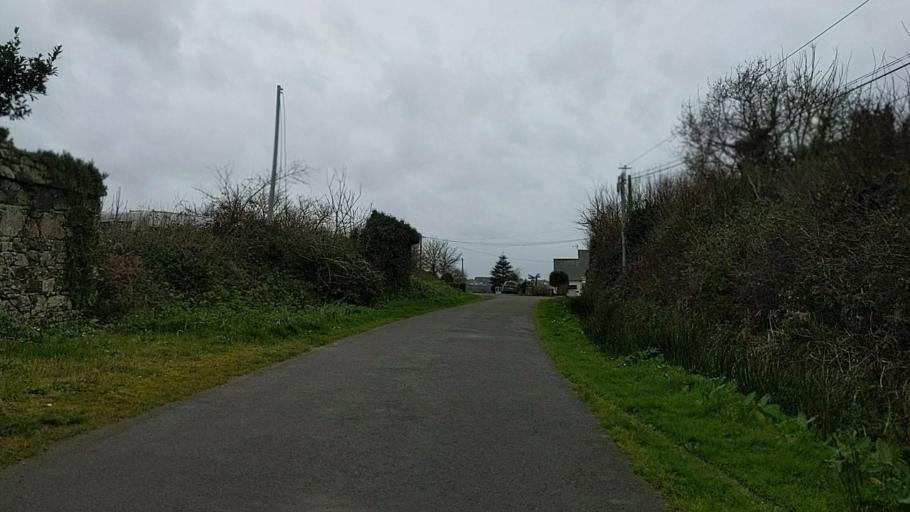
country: FR
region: Brittany
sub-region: Departement des Cotes-d'Armor
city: Plougrescant
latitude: 48.8356
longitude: -3.1841
